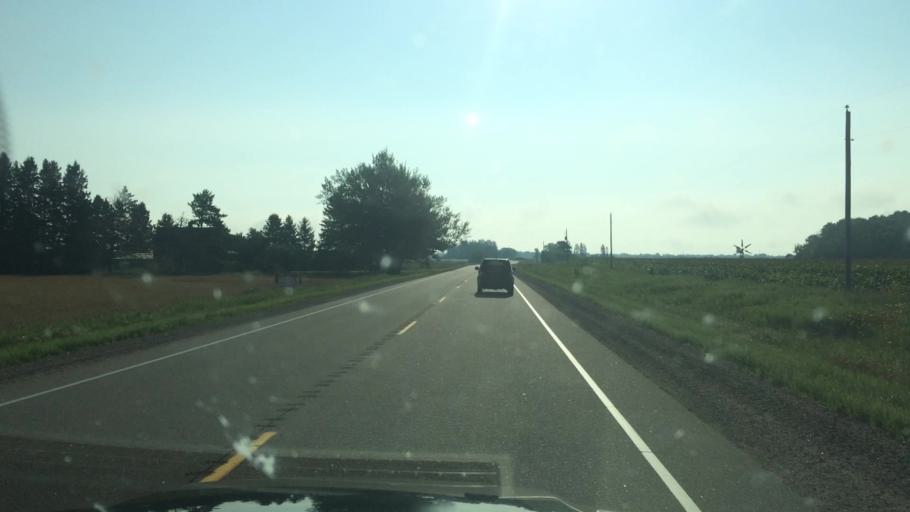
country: US
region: Wisconsin
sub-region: Langlade County
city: Antigo
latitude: 45.1401
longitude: -89.2032
